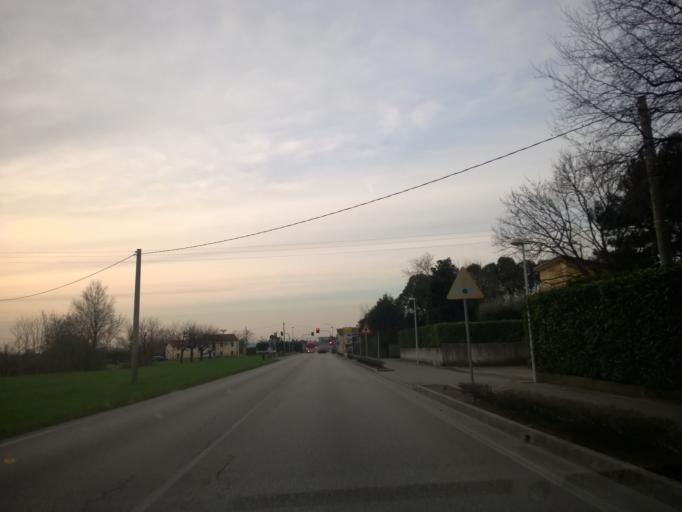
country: IT
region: Veneto
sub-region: Provincia di Vicenza
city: Centrale
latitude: 45.7260
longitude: 11.4663
